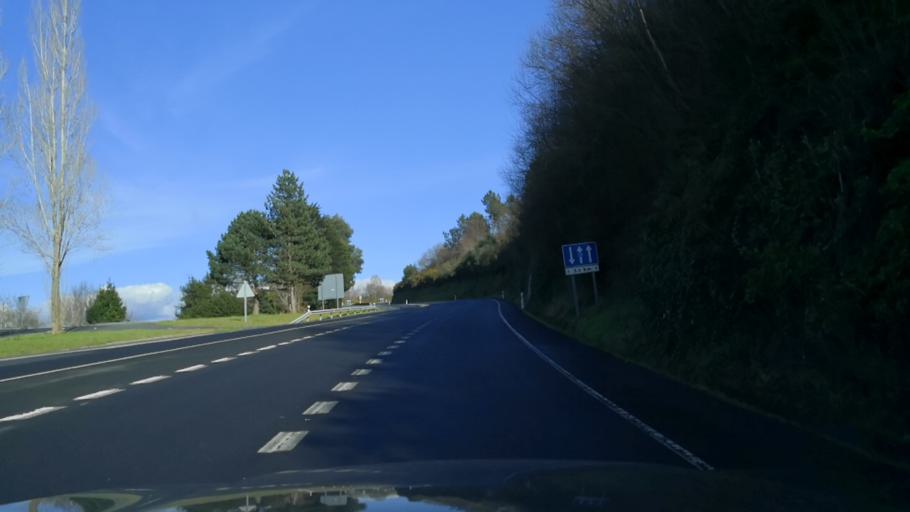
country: ES
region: Galicia
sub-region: Provincia da Coruna
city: Ribeira
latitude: 42.7133
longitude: -8.3782
